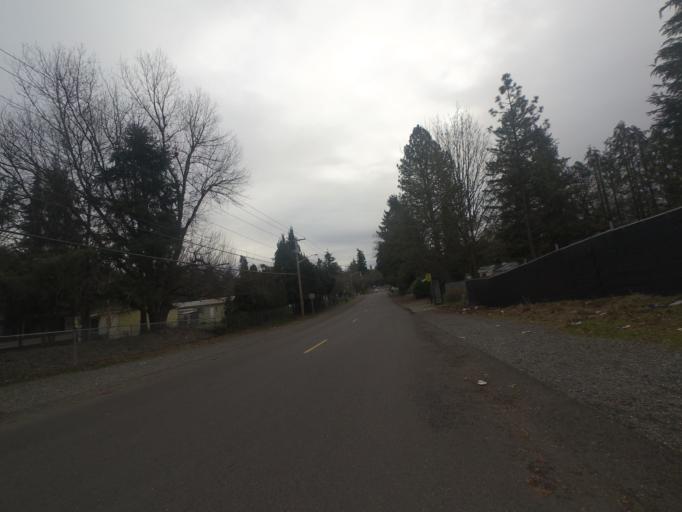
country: US
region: Washington
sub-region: Pierce County
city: McChord Air Force Base
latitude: 47.1248
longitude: -122.5278
